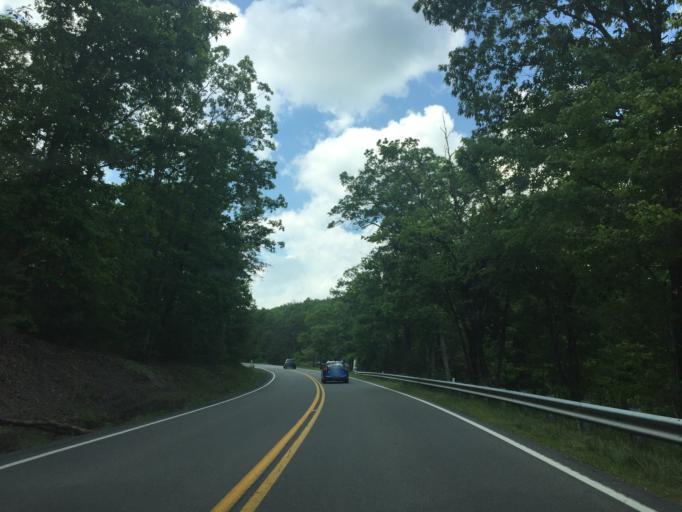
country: US
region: Virginia
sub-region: Shenandoah County
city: Strasburg
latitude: 39.0921
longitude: -78.4387
